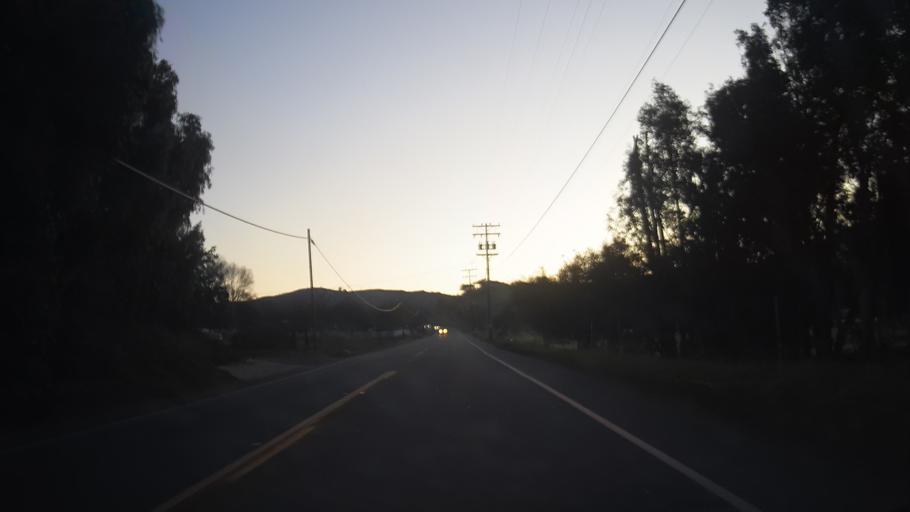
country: US
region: California
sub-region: San Diego County
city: Crest
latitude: 32.7902
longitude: -116.8415
